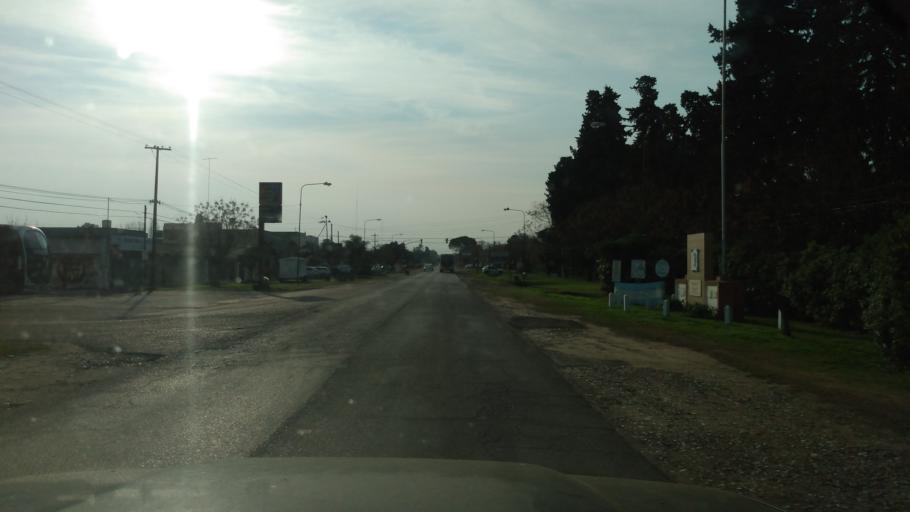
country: AR
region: Buenos Aires
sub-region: Partido de Lujan
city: Lujan
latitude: -34.5753
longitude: -59.1780
